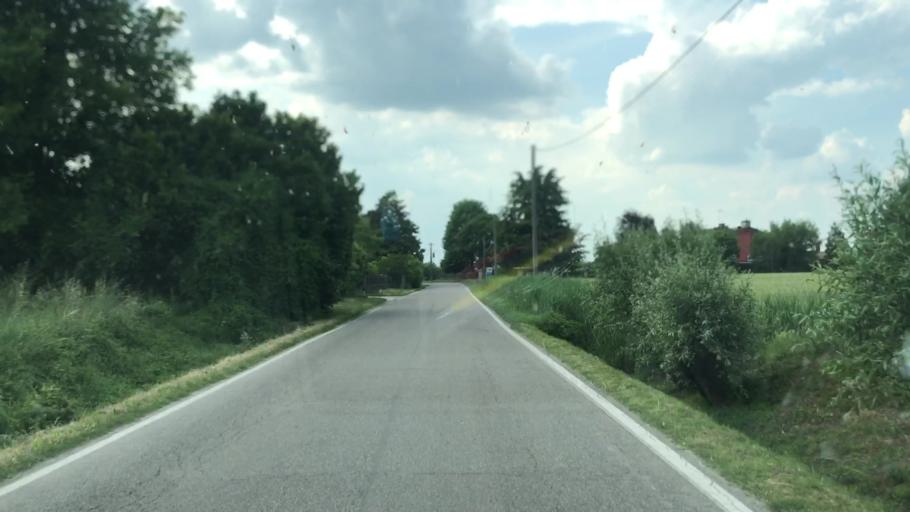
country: IT
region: Lombardy
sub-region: Provincia di Mantova
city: Castel Goffredo
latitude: 45.2924
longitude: 10.5014
